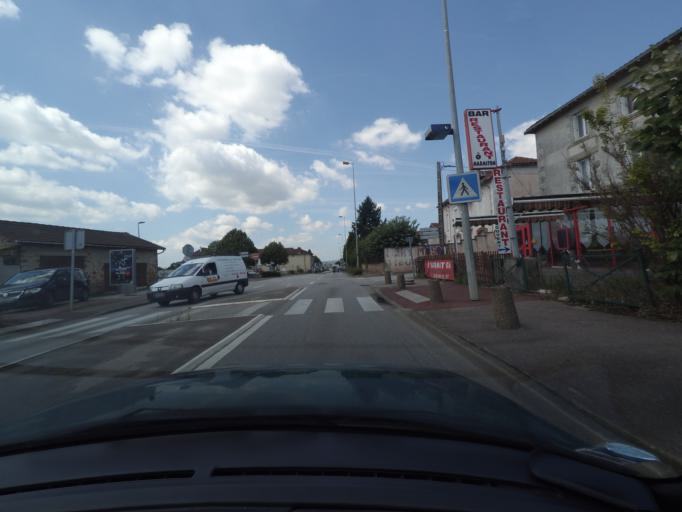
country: FR
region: Limousin
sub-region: Departement de la Haute-Vienne
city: Feytiat
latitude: 45.8154
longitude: 1.3145
